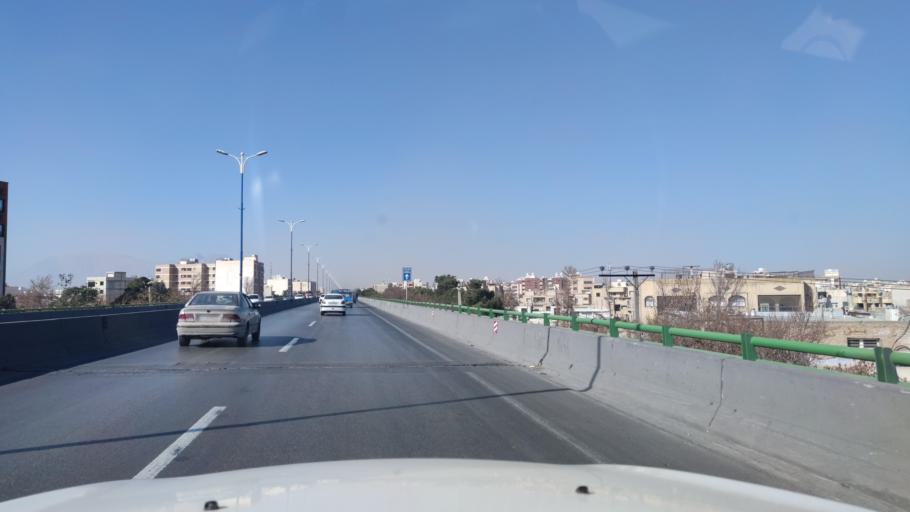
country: IR
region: Isfahan
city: Rehnan
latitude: 32.6869
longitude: 51.6348
